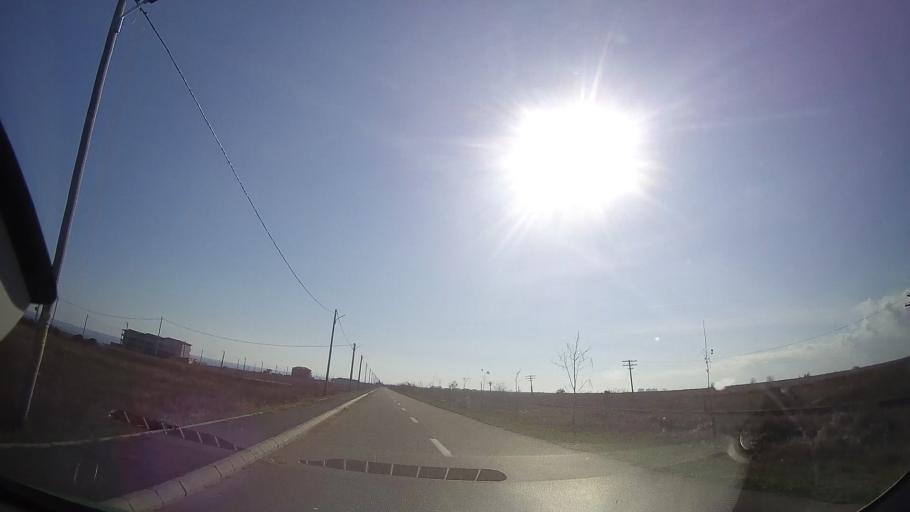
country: RO
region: Constanta
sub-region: Comuna Costinesti
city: Schitu
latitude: 43.9328
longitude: 28.6311
